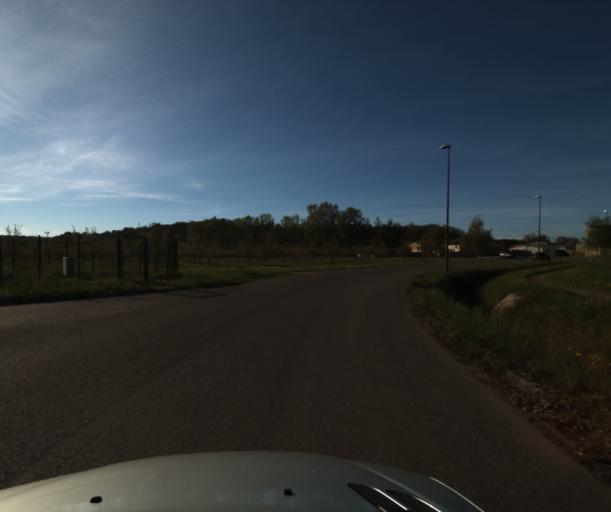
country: FR
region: Midi-Pyrenees
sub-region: Departement du Tarn-et-Garonne
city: Moissac
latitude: 44.1060
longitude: 1.1082
